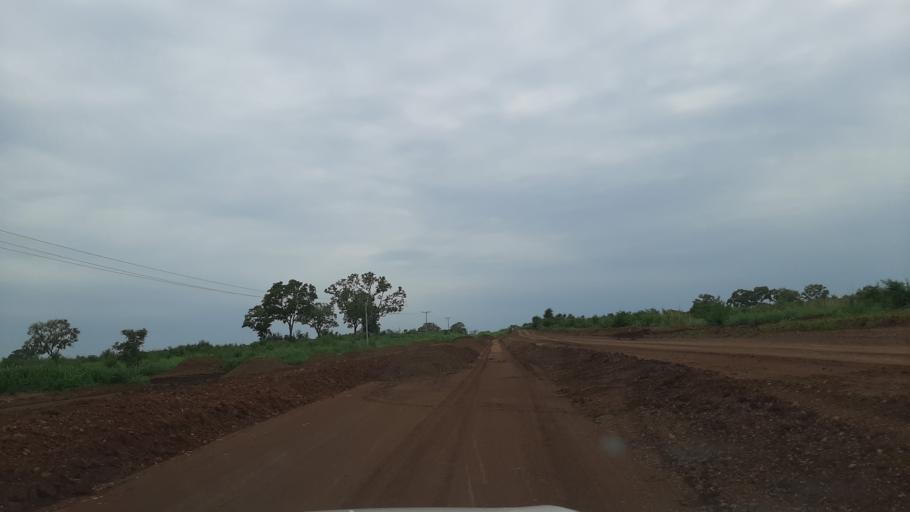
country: ET
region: Gambela
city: Gambela
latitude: 8.1812
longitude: 34.4936
